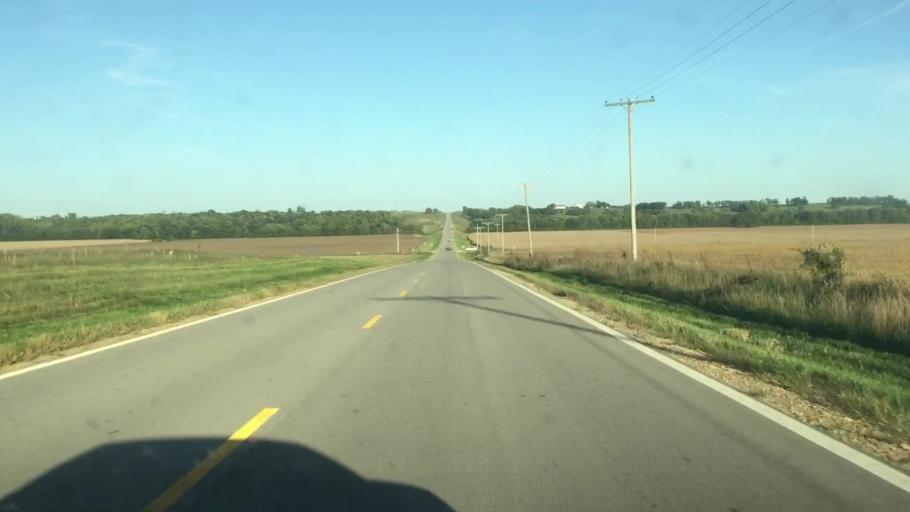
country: US
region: Kansas
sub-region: Brown County
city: Horton
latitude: 39.5875
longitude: -95.5681
